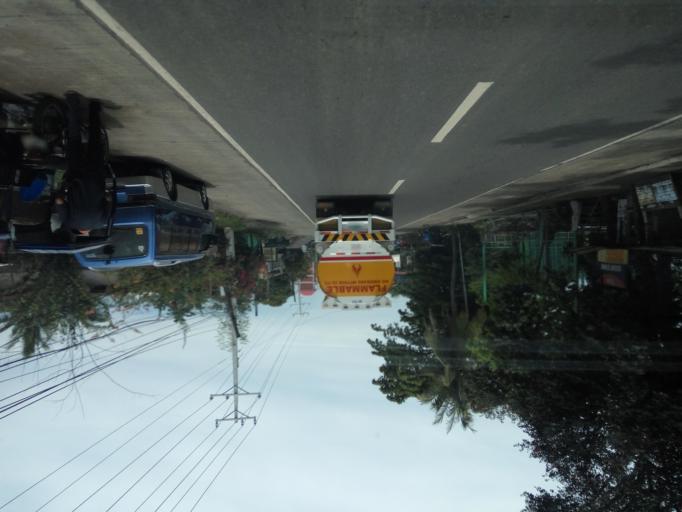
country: PH
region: Cagayan Valley
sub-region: Province of Isabela
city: Santiago
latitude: 16.6925
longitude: 121.5278
